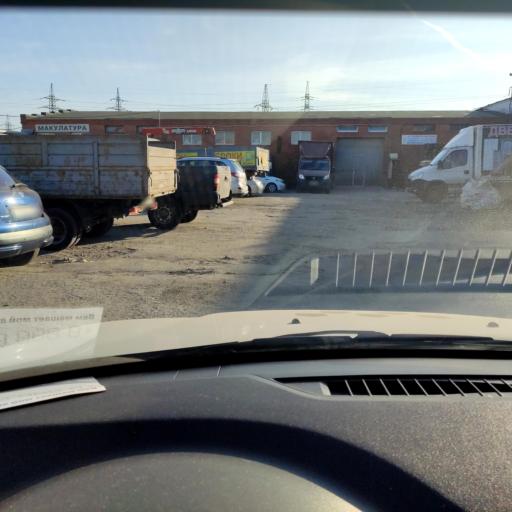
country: RU
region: Samara
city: Tol'yatti
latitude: 53.5315
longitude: 49.4487
